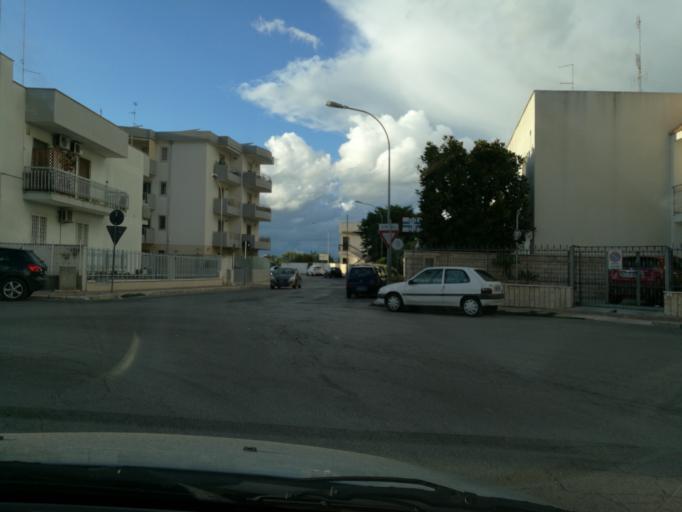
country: IT
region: Apulia
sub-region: Provincia di Bari
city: Valenzano
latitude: 41.0476
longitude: 16.8858
